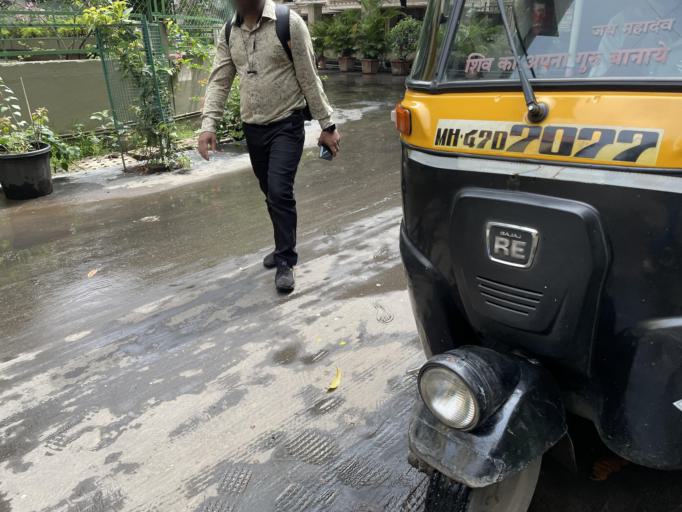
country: IN
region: Maharashtra
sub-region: Mumbai Suburban
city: Borivli
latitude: 19.2276
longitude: 72.8669
